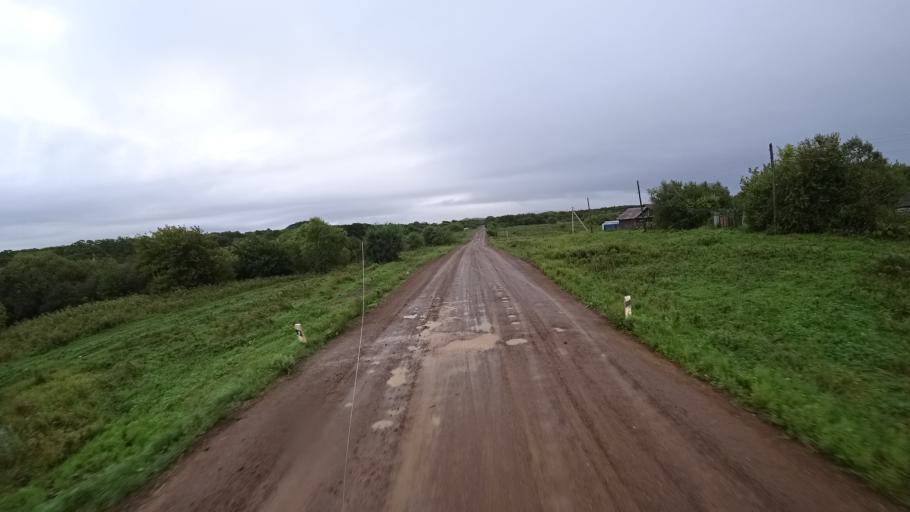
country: RU
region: Primorskiy
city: Monastyrishche
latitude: 44.2765
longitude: 132.4264
